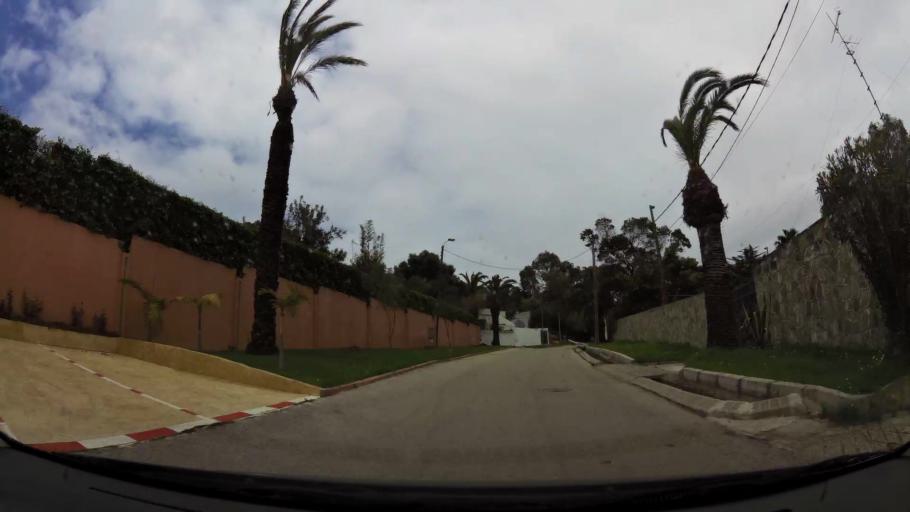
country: MA
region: Tanger-Tetouan
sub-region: Tanger-Assilah
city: Tangier
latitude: 35.7832
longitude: -5.8500
